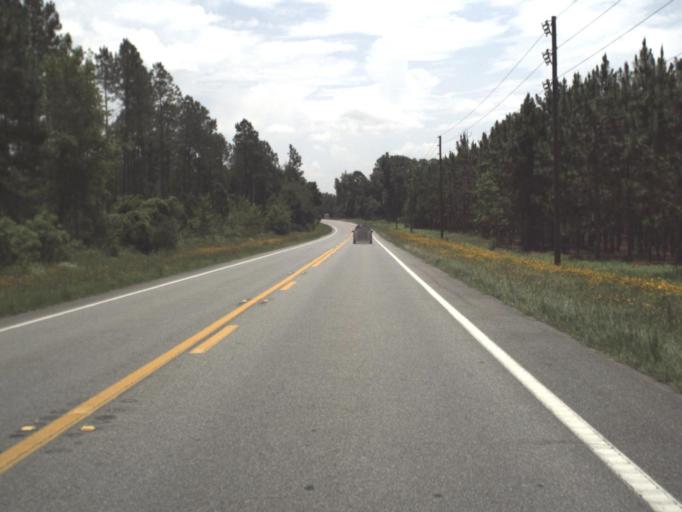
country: US
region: Florida
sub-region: Madison County
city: Madison
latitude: 30.4527
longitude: -83.3497
